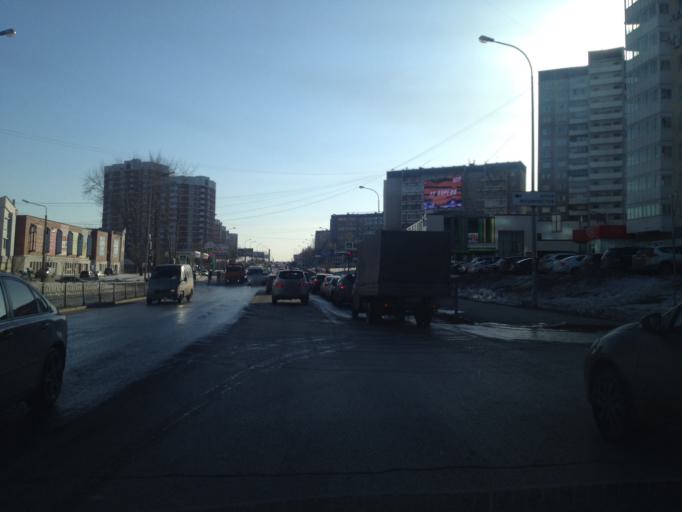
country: RU
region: Sverdlovsk
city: Yekaterinburg
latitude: 56.8541
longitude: 60.5730
